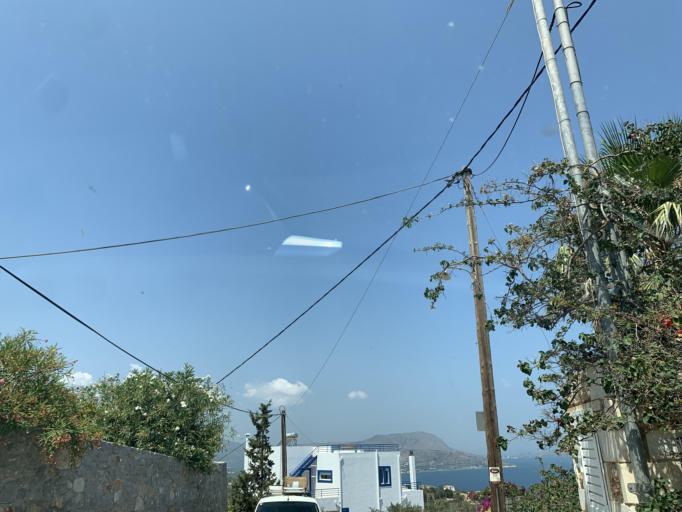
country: GR
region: Crete
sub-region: Nomos Chanias
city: Kalivai
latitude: 35.4504
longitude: 24.2298
